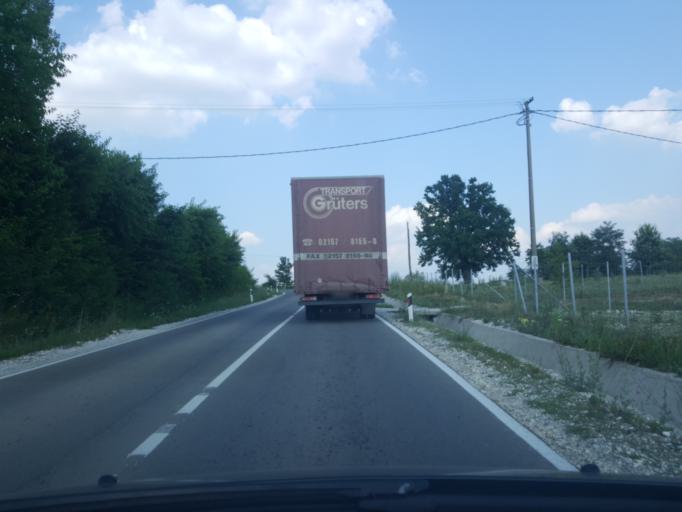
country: RS
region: Central Serbia
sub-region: Sumadijski Okrug
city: Topola
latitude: 44.2043
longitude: 20.6144
